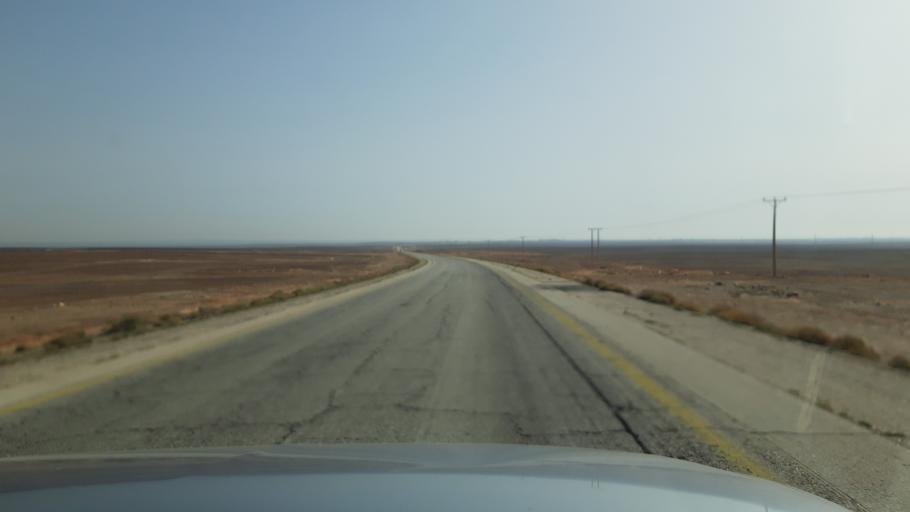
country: JO
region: Amman
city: Al Azraq ash Shamali
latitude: 31.8541
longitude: 36.6845
